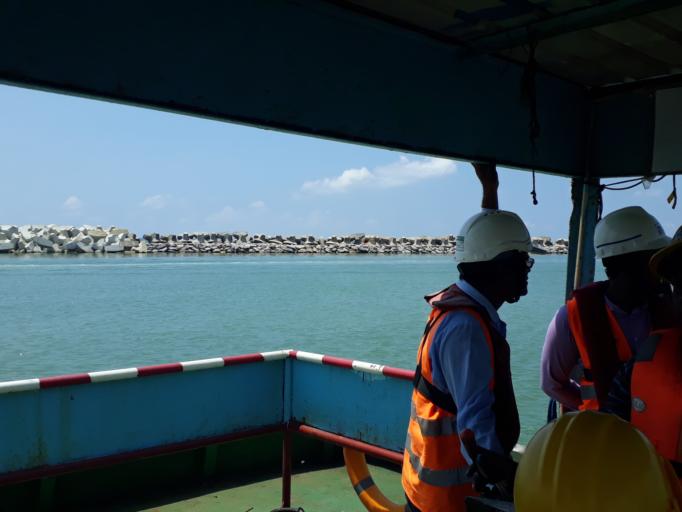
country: LK
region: Western
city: Colombo
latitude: 6.9271
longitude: 79.8237
